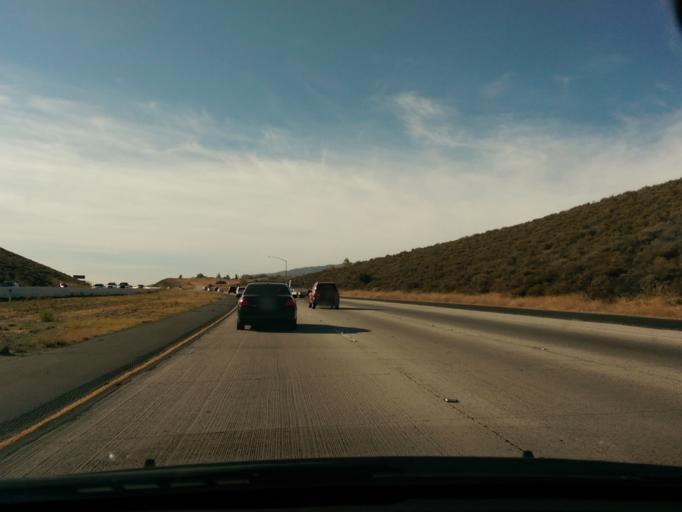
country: US
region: California
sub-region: Riverside County
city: El Cerrito
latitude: 33.7720
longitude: -117.4845
